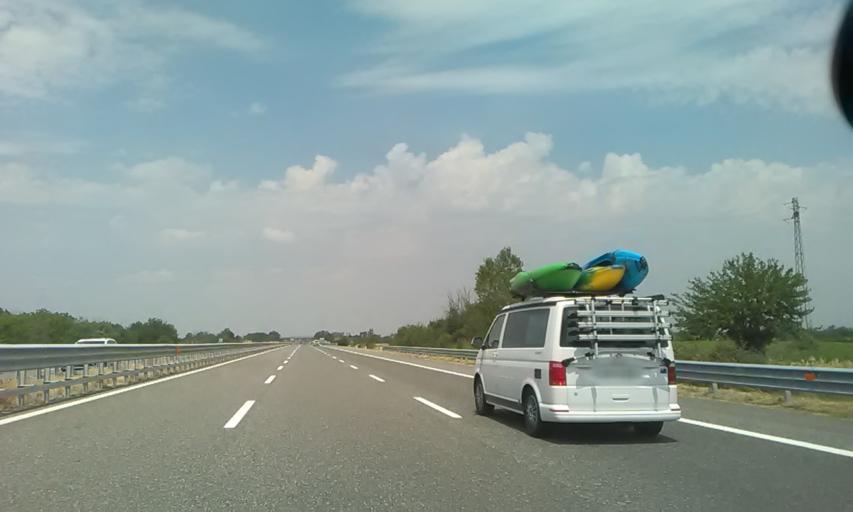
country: IT
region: Piedmont
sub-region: Provincia di Alessandria
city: Castelspina
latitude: 44.7977
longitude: 8.6086
